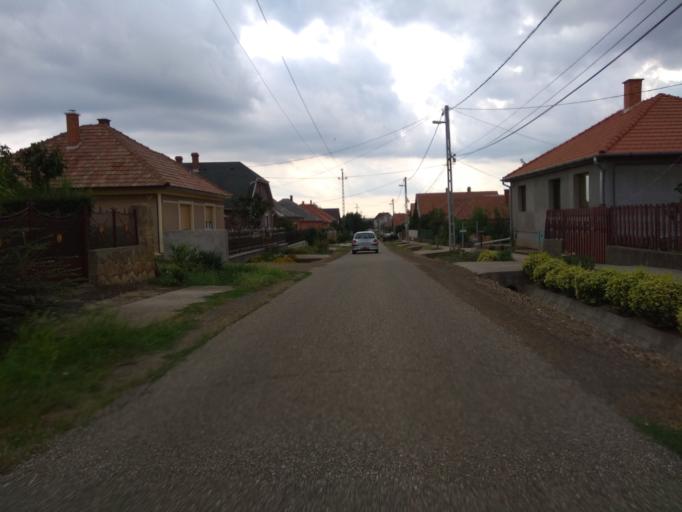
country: HU
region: Borsod-Abauj-Zemplen
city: Bekecs
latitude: 48.1513
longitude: 21.1624
